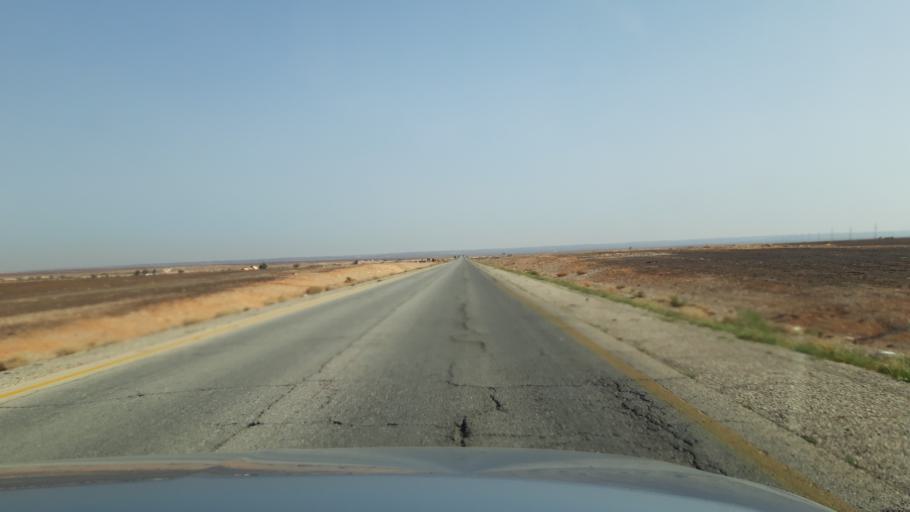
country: JO
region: Amman
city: Al Azraq ash Shamali
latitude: 31.7901
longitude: 36.5822
